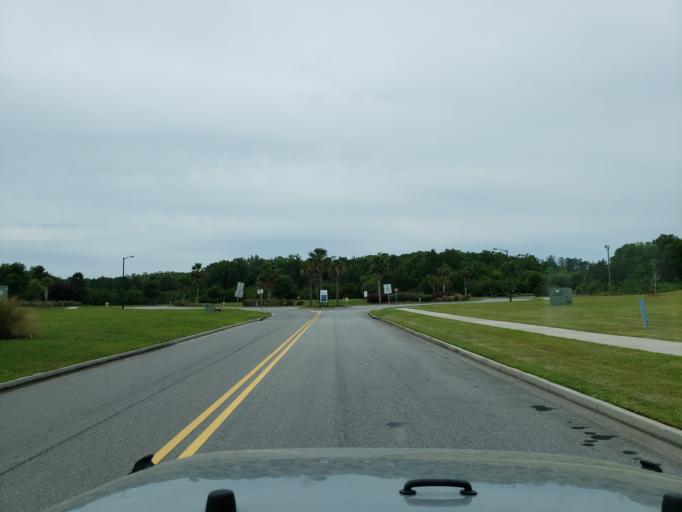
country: US
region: Georgia
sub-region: Chatham County
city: Port Wentworth
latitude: 32.2169
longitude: -81.1944
